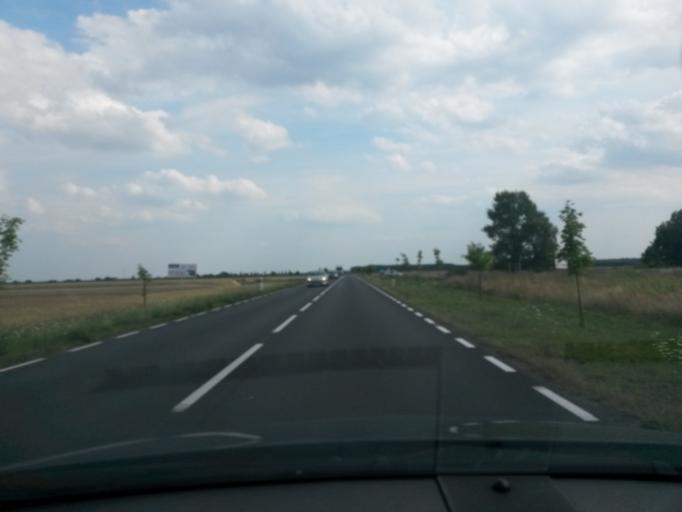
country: PL
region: Greater Poland Voivodeship
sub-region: Powiat poznanski
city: Kornik
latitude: 52.2360
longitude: 17.0606
